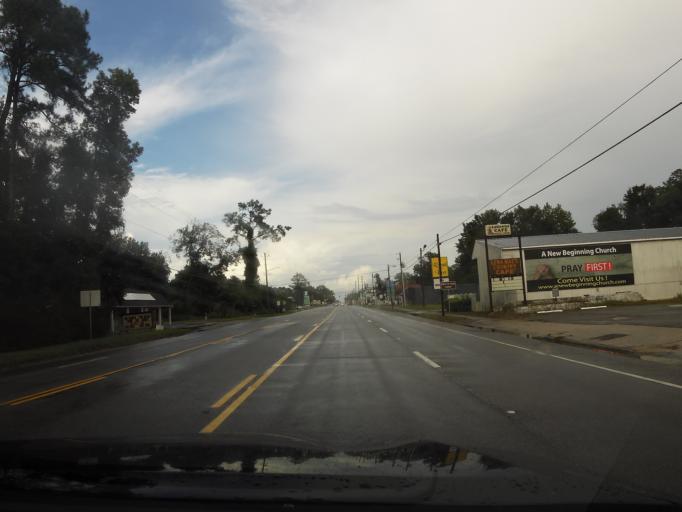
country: US
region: Georgia
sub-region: Long County
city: Ludowici
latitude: 31.7118
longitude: -81.7485
